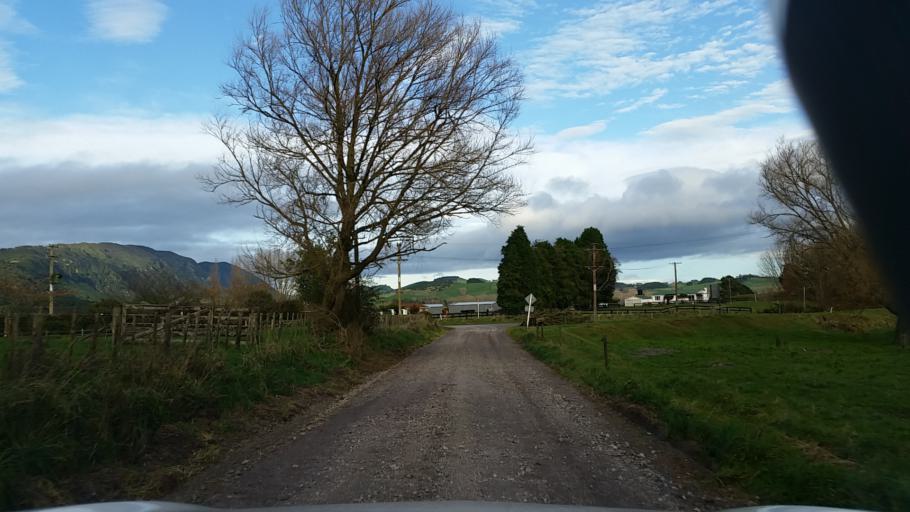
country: NZ
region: Bay of Plenty
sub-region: Rotorua District
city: Rotorua
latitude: -38.3240
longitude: 176.2952
